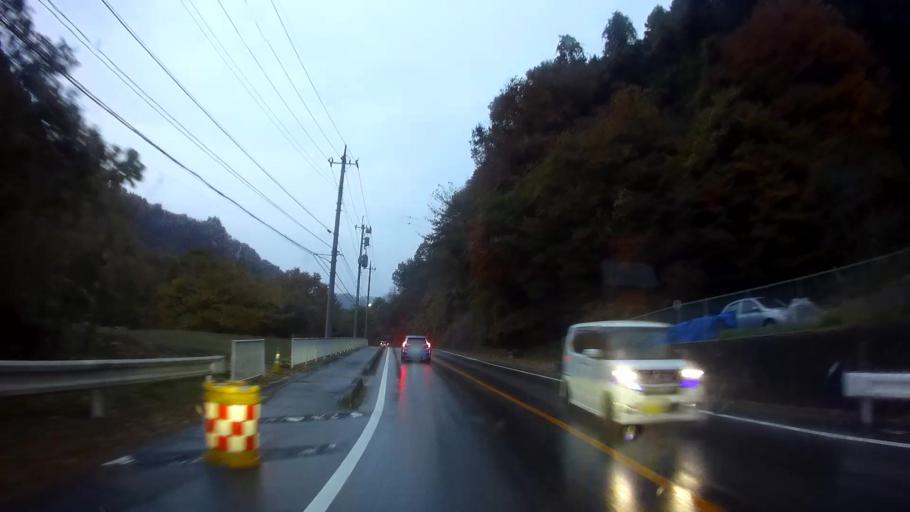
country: JP
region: Gunma
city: Nakanojomachi
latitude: 36.5178
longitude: 138.7786
